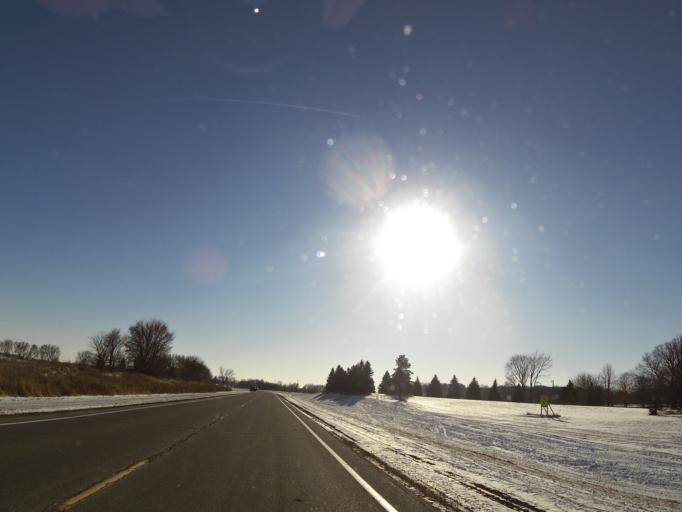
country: US
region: Minnesota
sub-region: Scott County
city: Prior Lake
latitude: 44.6488
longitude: -93.5001
